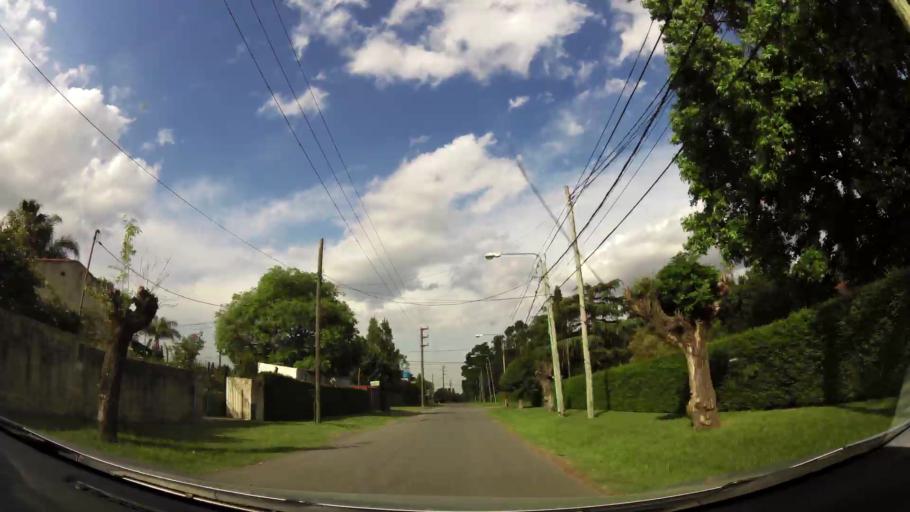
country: AR
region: Buenos Aires
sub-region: Partido de Tigre
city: Tigre
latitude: -34.4764
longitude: -58.6532
